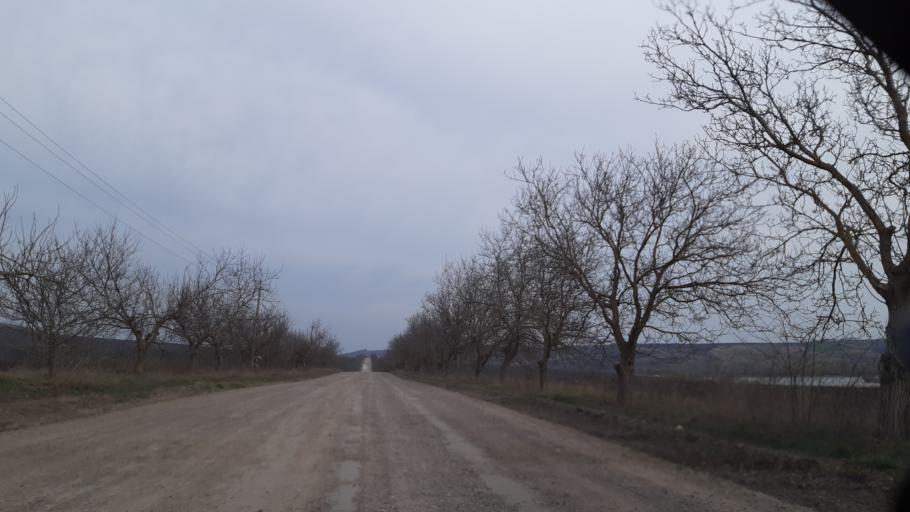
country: MD
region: Soldanesti
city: Soldanesti
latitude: 47.7002
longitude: 28.7235
